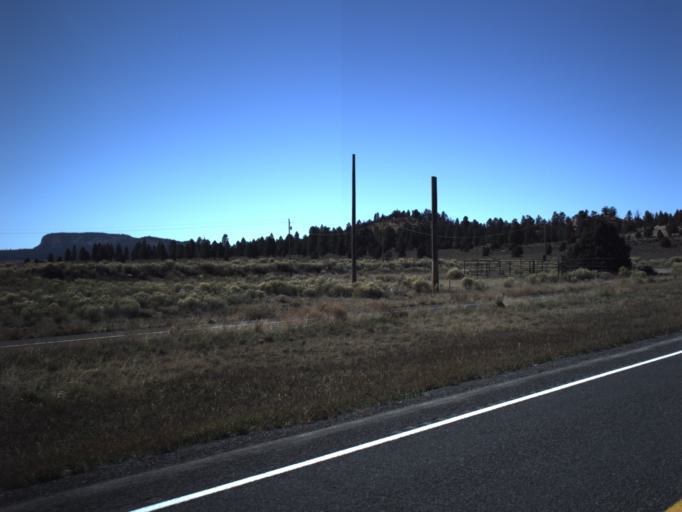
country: US
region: Utah
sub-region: Garfield County
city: Panguitch
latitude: 37.7037
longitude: -112.2001
